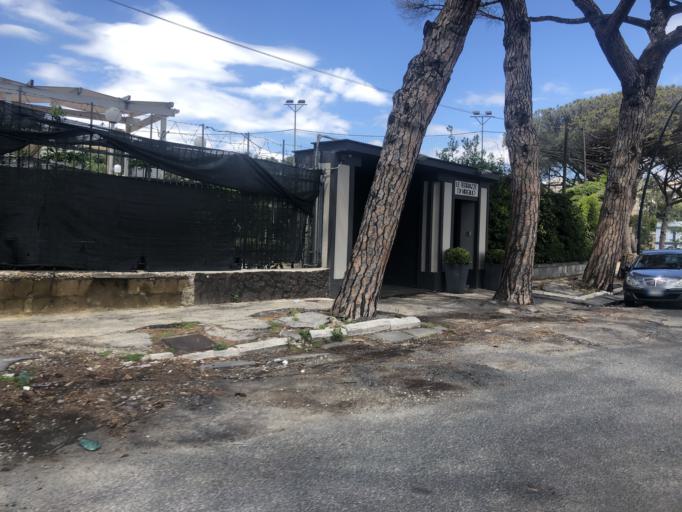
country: IT
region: Campania
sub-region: Provincia di Napoli
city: Bagnoli
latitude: 40.7994
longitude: 14.1871
